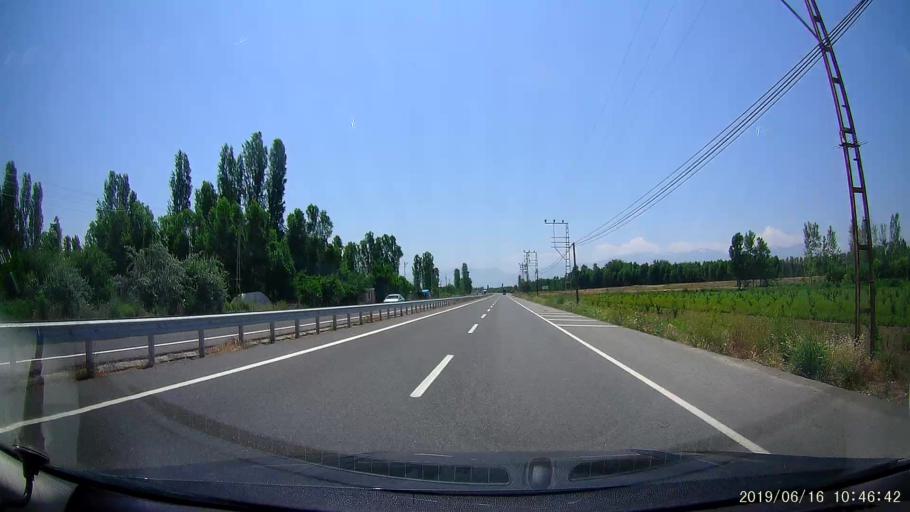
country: AM
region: Armavir
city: Shenavan
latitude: 40.0191
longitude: 43.8809
